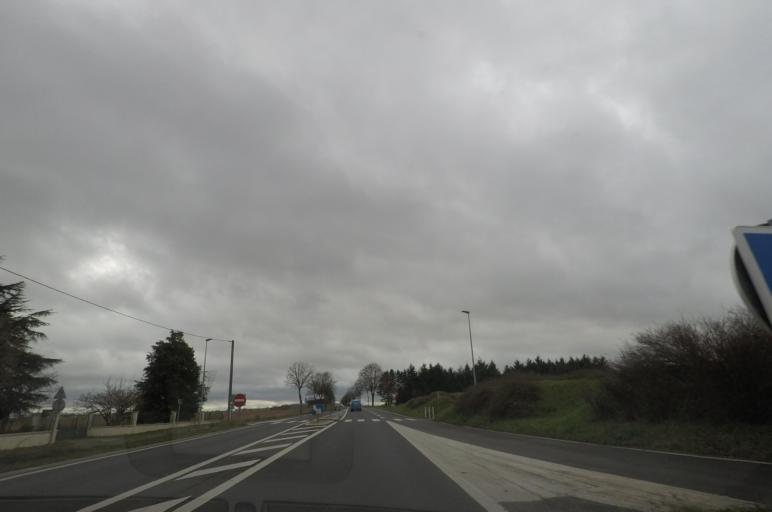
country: FR
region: Centre
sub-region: Departement du Loir-et-Cher
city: Saint-Sulpice-de-Pommeray
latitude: 47.6454
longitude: 1.2763
